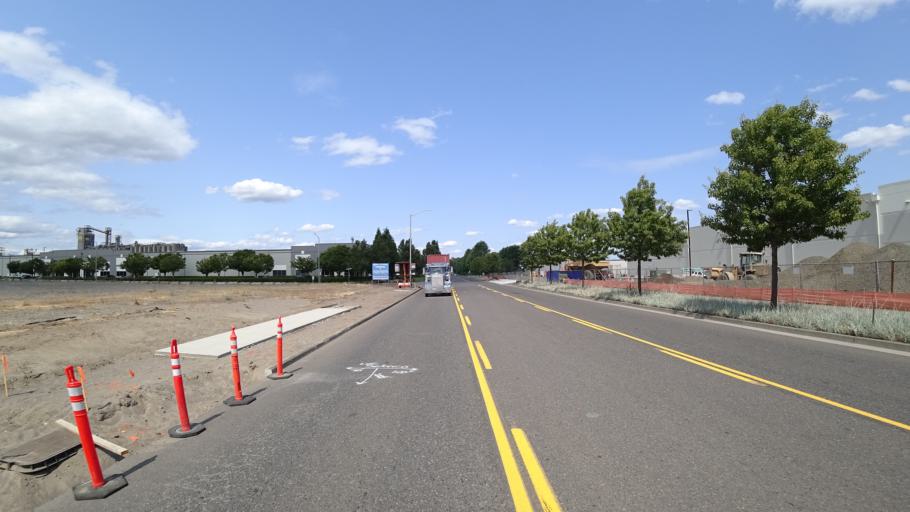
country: US
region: Washington
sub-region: Clark County
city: Lake Shore
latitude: 45.6345
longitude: -122.7701
